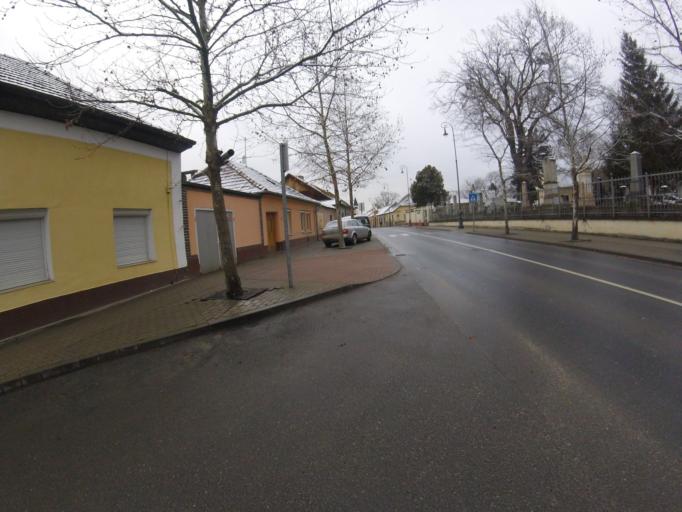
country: HU
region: Komarom-Esztergom
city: Esztergom
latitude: 47.7878
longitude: 18.7459
